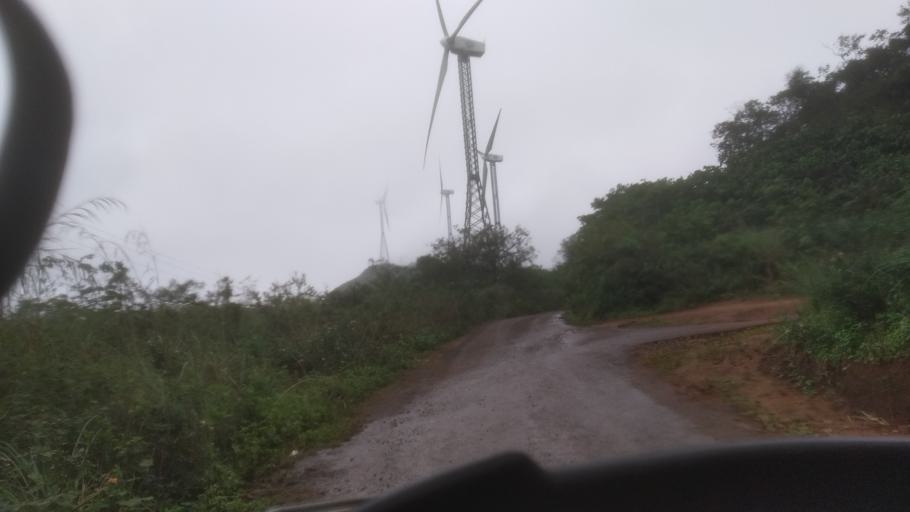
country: IN
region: Tamil Nadu
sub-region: Theni
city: Kombai
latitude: 9.8901
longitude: 77.2222
